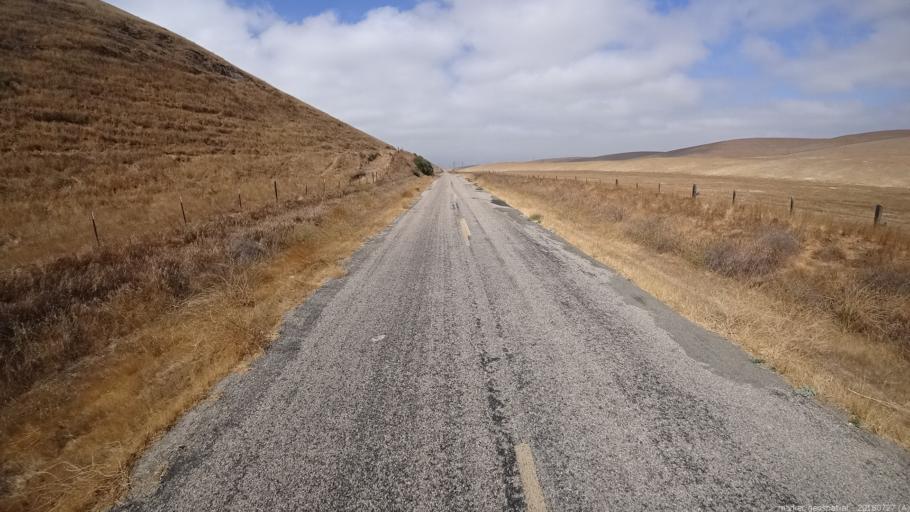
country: US
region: California
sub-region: Monterey County
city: King City
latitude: 36.2310
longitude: -121.0508
